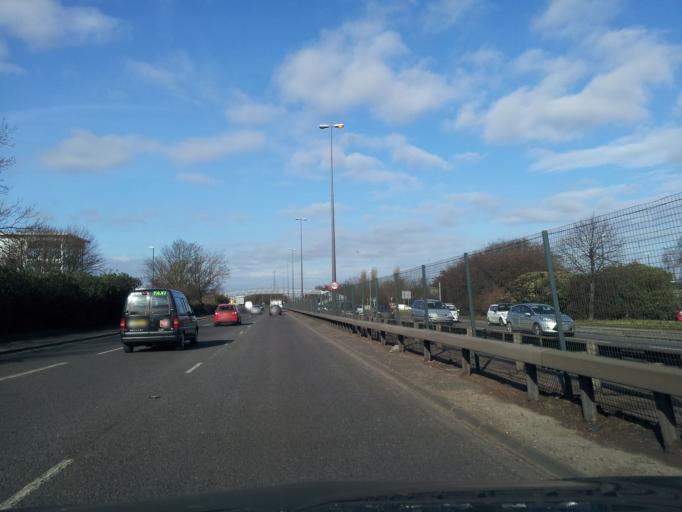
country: GB
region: England
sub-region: Nottingham
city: Nottingham
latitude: 52.9323
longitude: -1.1712
